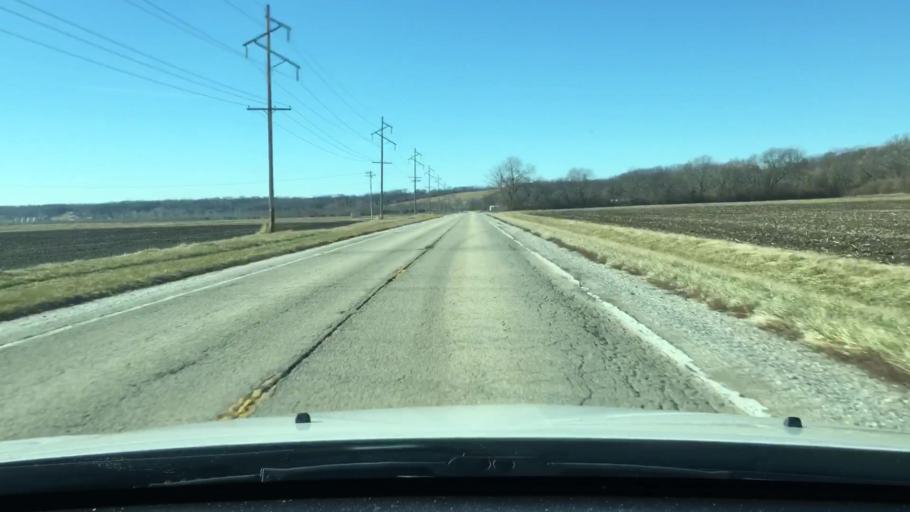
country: US
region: Illinois
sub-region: Fulton County
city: Astoria
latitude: 40.1753
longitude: -90.2662
